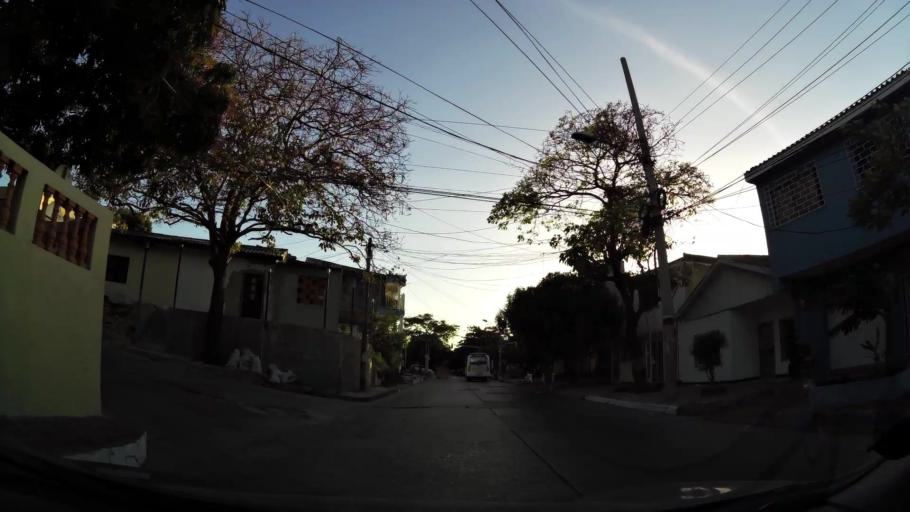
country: CO
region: Atlantico
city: Barranquilla
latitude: 10.9786
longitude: -74.7963
